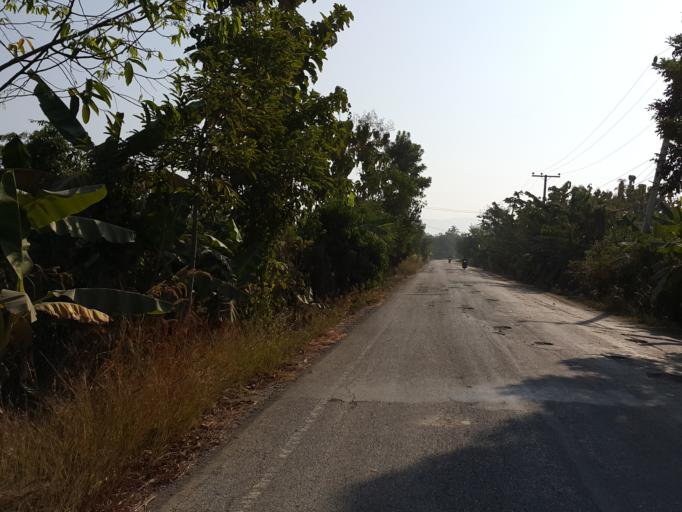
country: TH
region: Chiang Mai
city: San Kamphaeng
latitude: 18.6975
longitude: 99.1091
